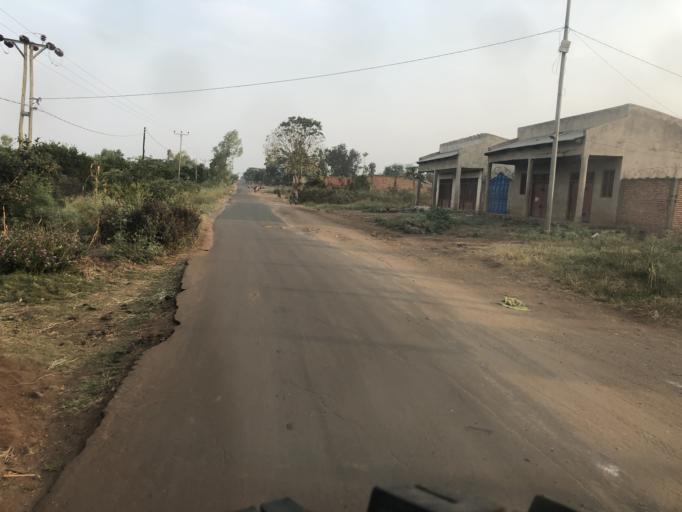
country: BI
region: Cibitoke
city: Cibitoke
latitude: -2.7185
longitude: 29.0047
